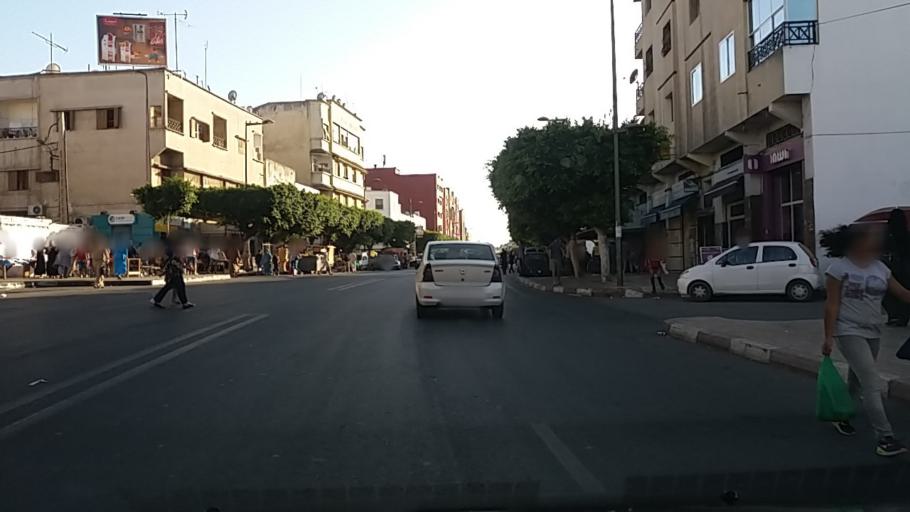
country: MA
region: Gharb-Chrarda-Beni Hssen
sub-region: Kenitra Province
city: Kenitra
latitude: 34.2661
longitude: -6.5636
